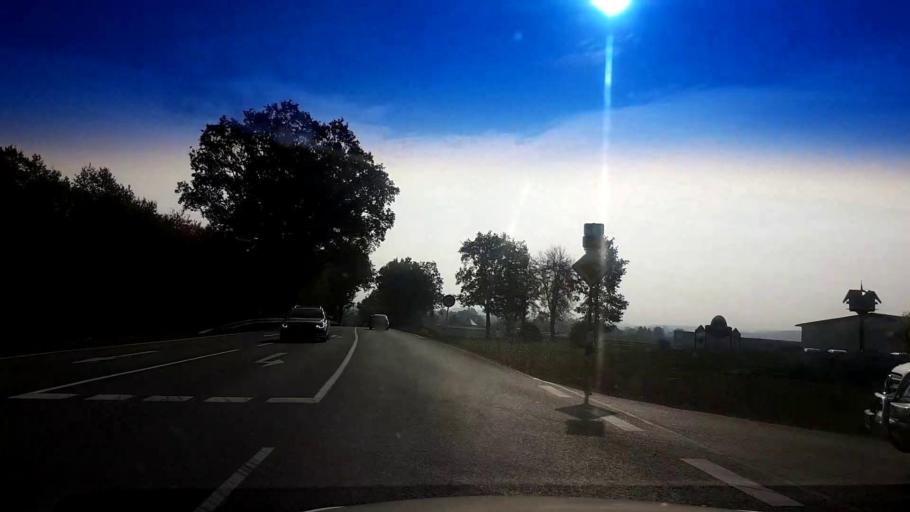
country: DE
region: Bavaria
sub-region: Upper Franconia
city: Himmelkron
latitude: 50.0588
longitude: 11.6071
